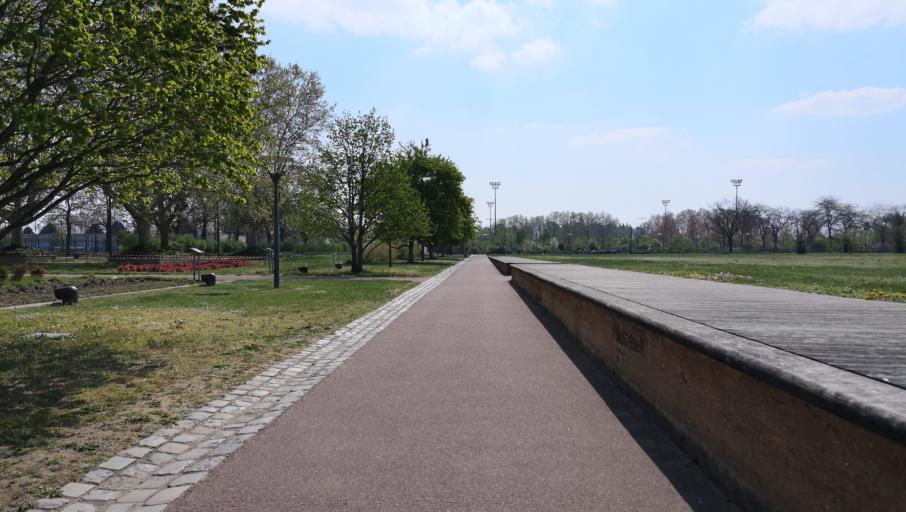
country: FR
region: Rhone-Alpes
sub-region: Departement du Rhone
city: La Mulatiere
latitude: 45.7228
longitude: 4.8242
